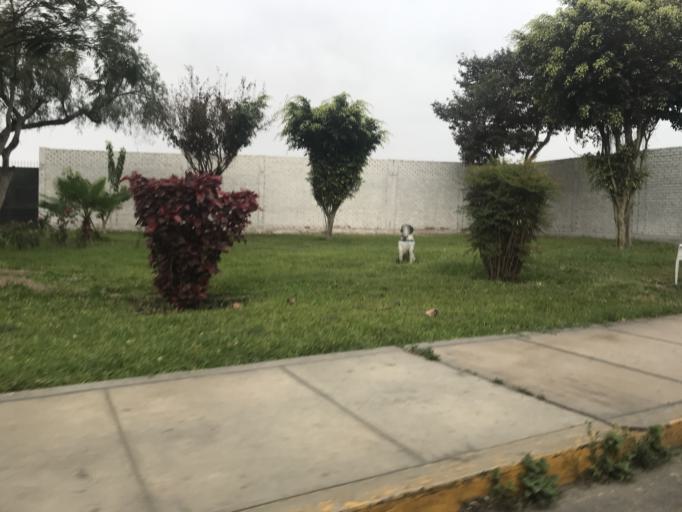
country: PE
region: Callao
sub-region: Callao
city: Callao
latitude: -12.0675
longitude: -77.0924
